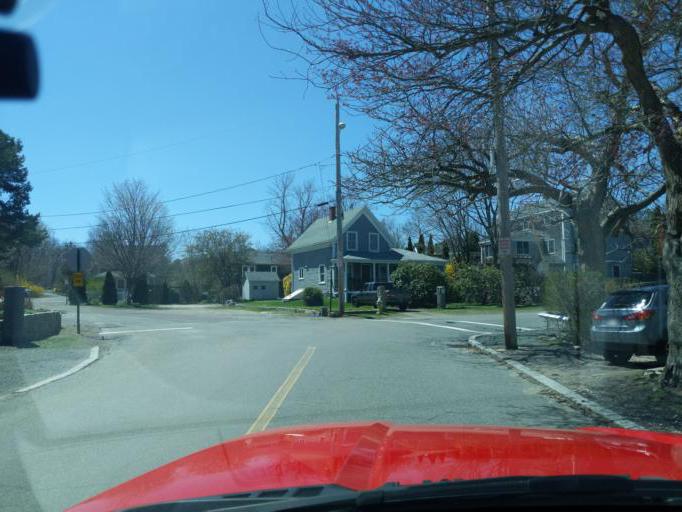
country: US
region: Massachusetts
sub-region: Essex County
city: Rockport
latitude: 42.6737
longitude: -70.6312
